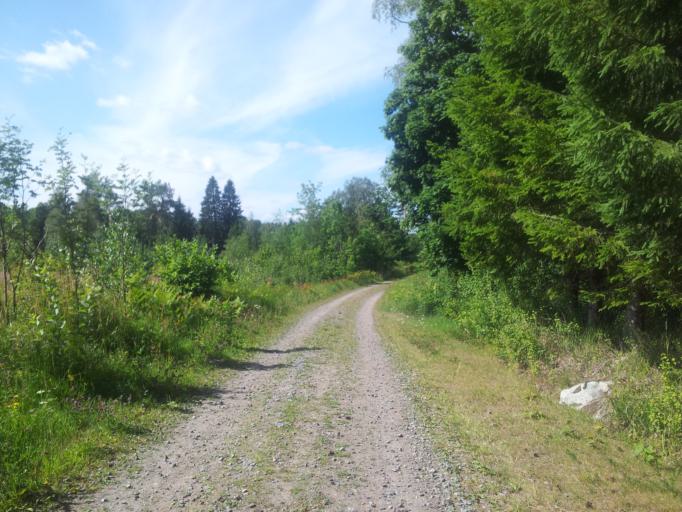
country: SE
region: Stockholm
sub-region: Norrtalje Kommun
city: Nykvarn
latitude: 59.8956
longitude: 18.2460
